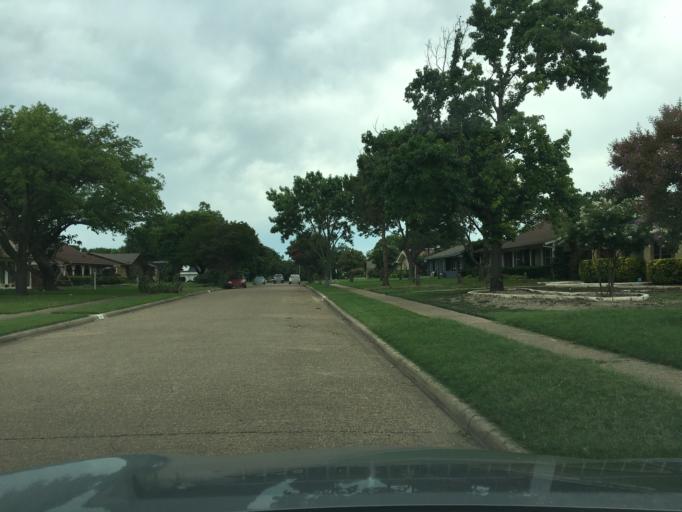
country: US
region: Texas
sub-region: Dallas County
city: Richardson
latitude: 32.9342
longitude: -96.7014
